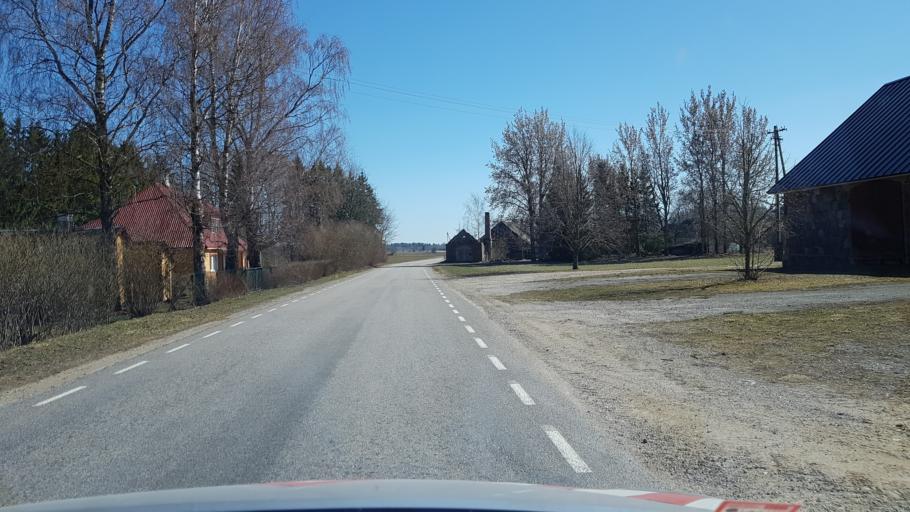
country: EE
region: Laeaene-Virumaa
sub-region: Vaeike-Maarja vald
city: Vaike-Maarja
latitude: 59.1124
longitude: 26.3720
